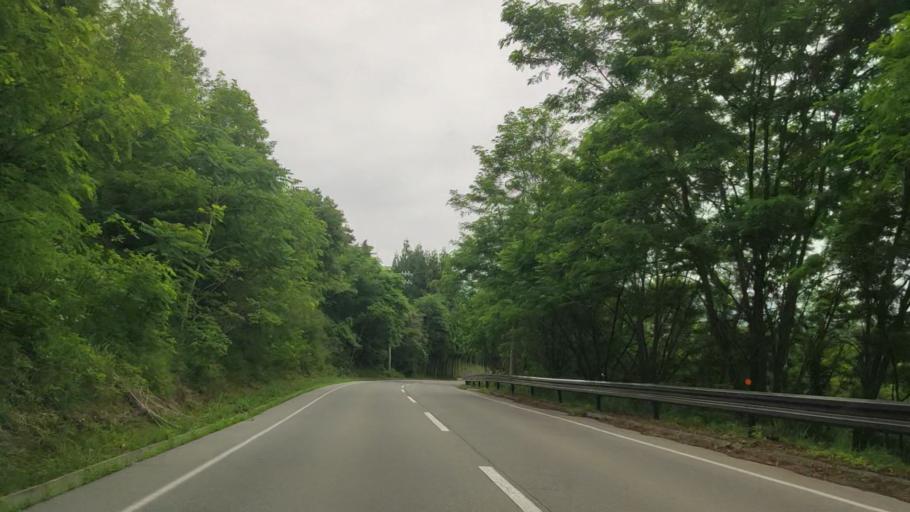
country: JP
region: Nagano
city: Kamimaruko
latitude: 36.3187
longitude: 138.3334
